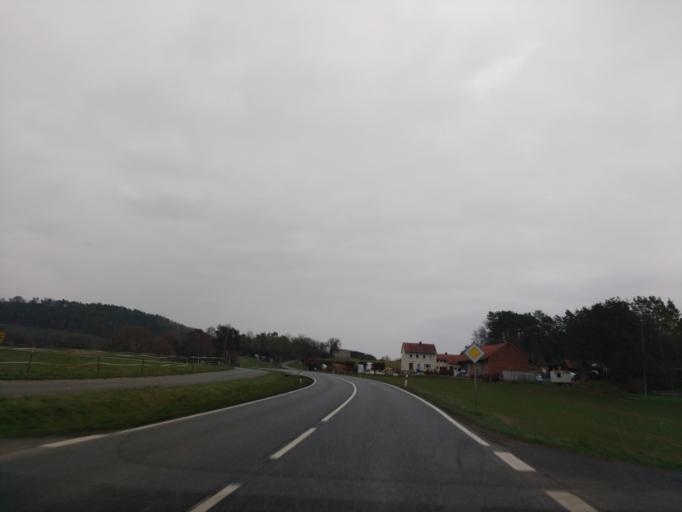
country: DE
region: Hesse
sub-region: Regierungsbezirk Kassel
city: Alheim
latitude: 51.0612
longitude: 9.6261
